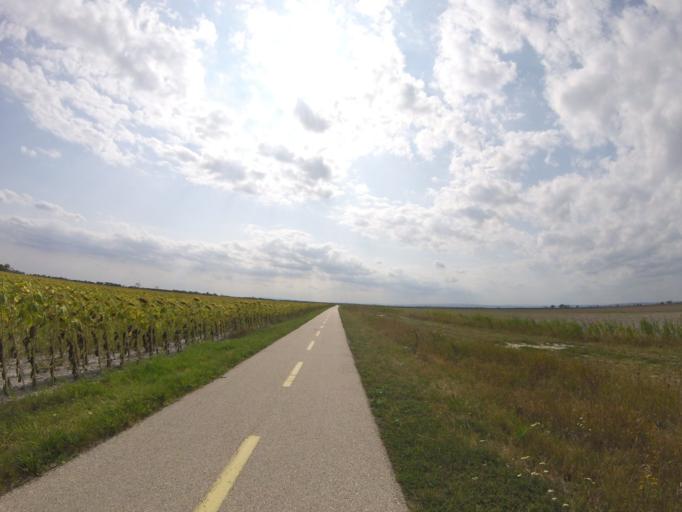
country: AT
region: Burgenland
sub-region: Politischer Bezirk Neusiedl am See
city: Apetlon
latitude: 47.7078
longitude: 16.8589
